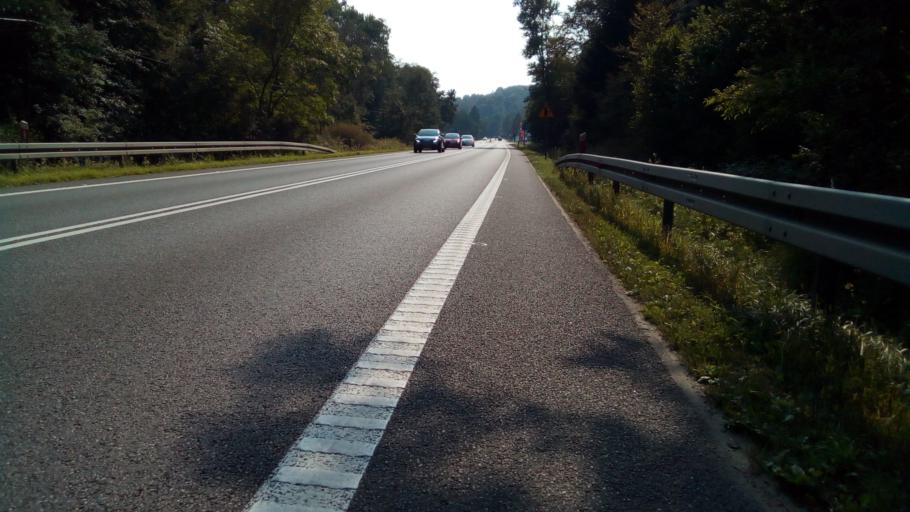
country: PL
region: Subcarpathian Voivodeship
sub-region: Powiat strzyzowski
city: Jawornik
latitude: 49.8284
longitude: 21.8780
